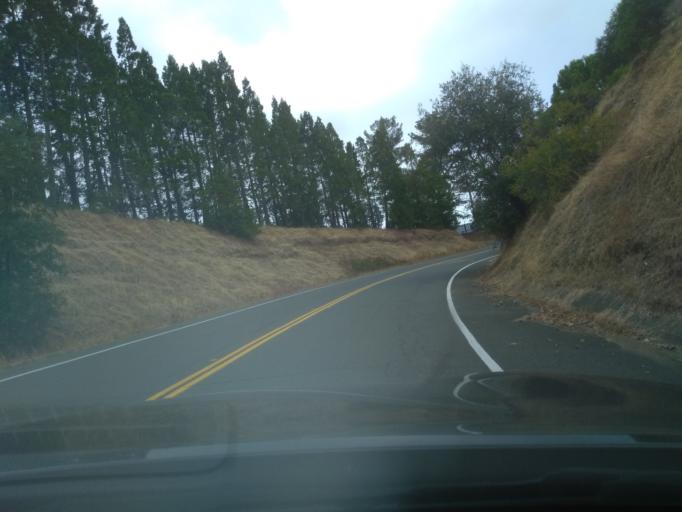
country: US
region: California
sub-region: Mendocino County
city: Ukiah
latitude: 39.2019
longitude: -123.1887
